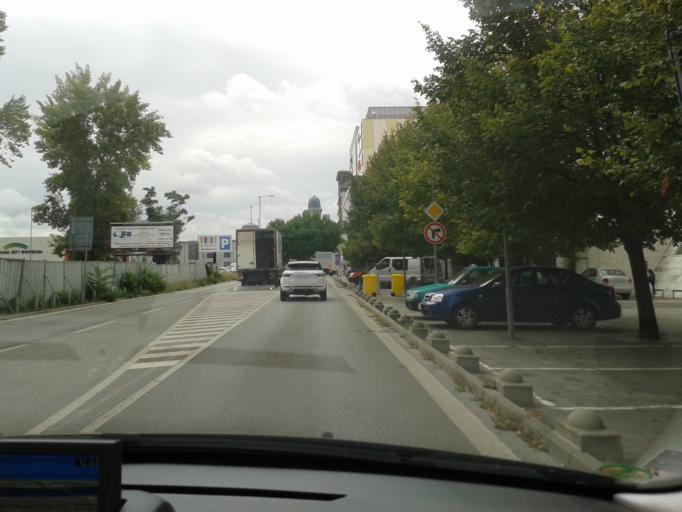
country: SK
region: Bratislavsky
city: Bratislava
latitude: 48.1417
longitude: 17.1249
